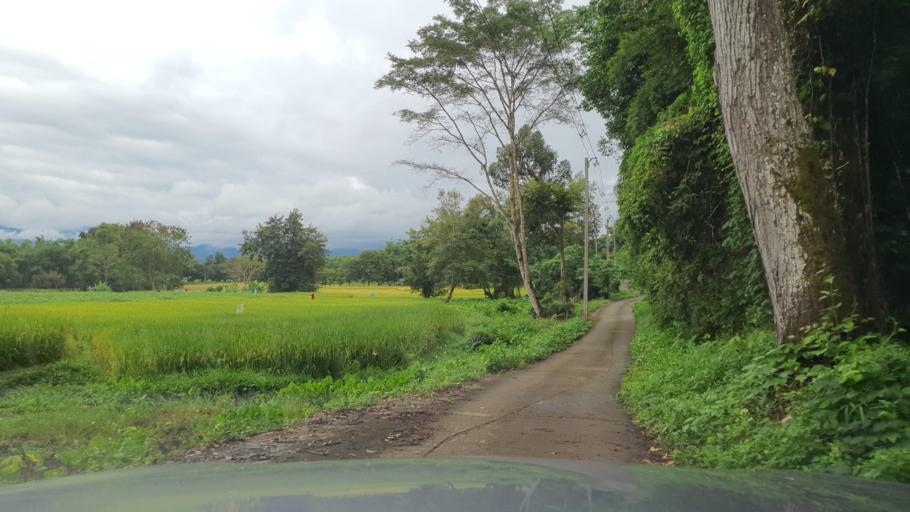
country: TH
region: Chiang Mai
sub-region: Amphoe Chiang Dao
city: Chiang Dao
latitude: 19.3375
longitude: 98.9268
